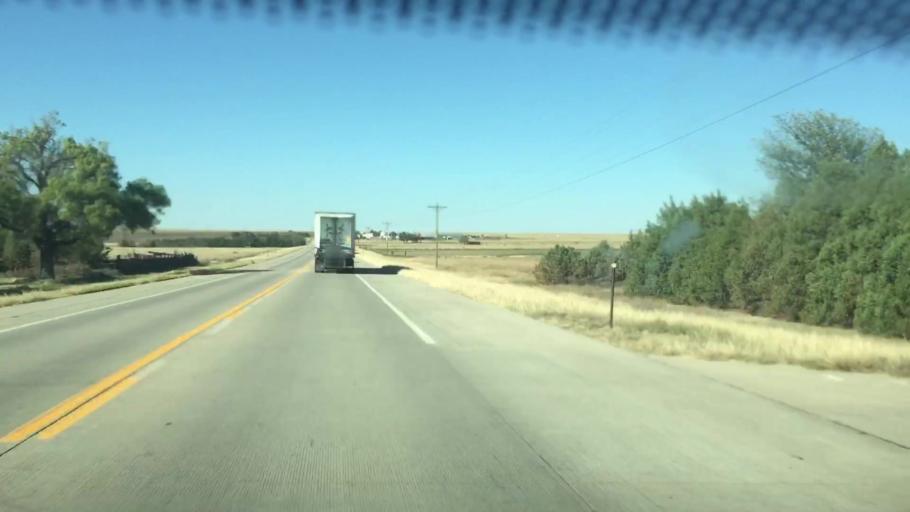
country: US
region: Colorado
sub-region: Kiowa County
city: Eads
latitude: 38.4548
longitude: -102.7306
